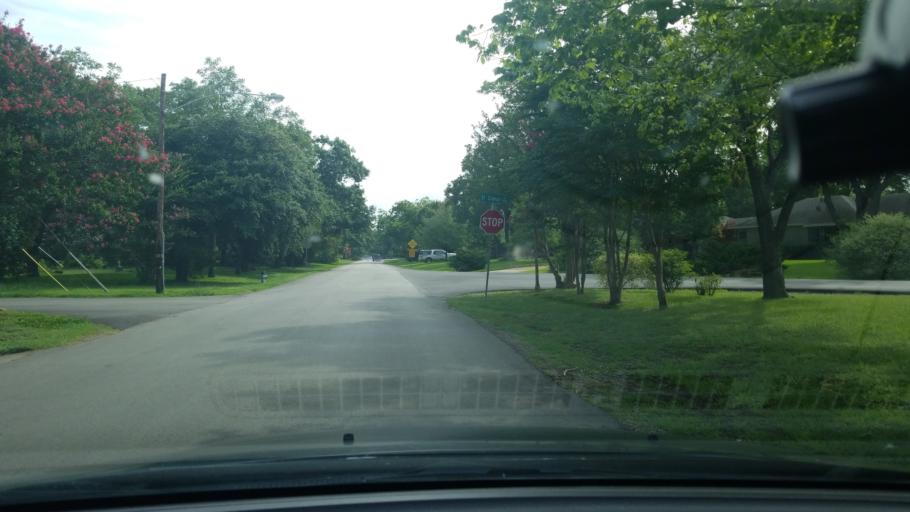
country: US
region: Texas
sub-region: Dallas County
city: Highland Park
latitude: 32.8284
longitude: -96.7025
